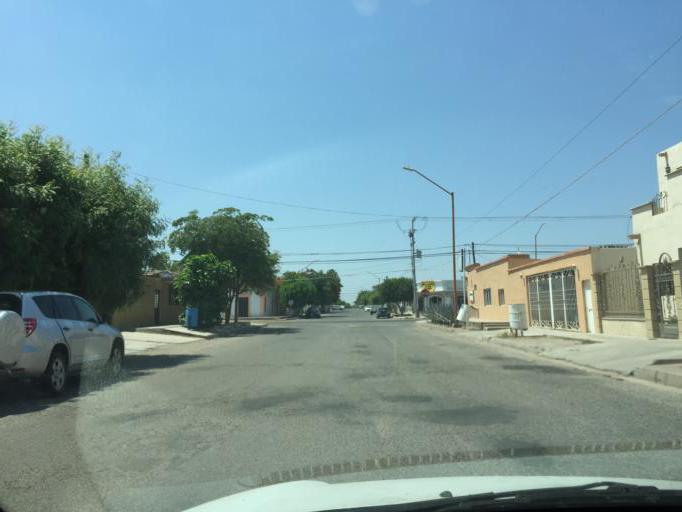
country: MX
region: Sonora
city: Navojoa
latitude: 27.0818
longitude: -109.4574
